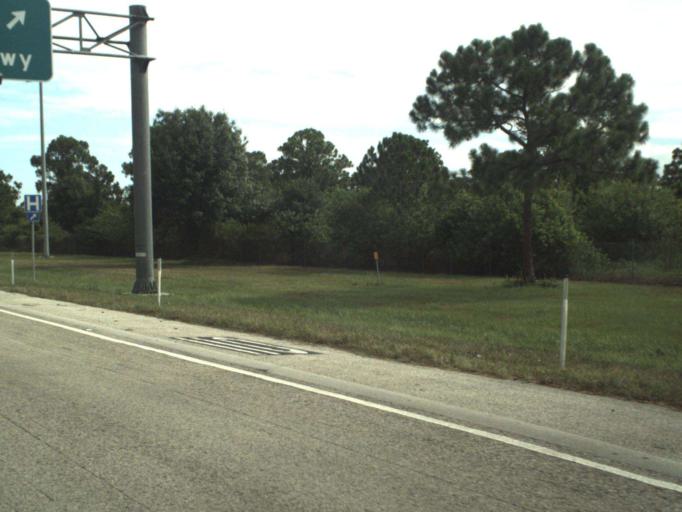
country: US
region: Florida
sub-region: Martin County
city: Palm City
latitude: 27.1570
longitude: -80.3874
